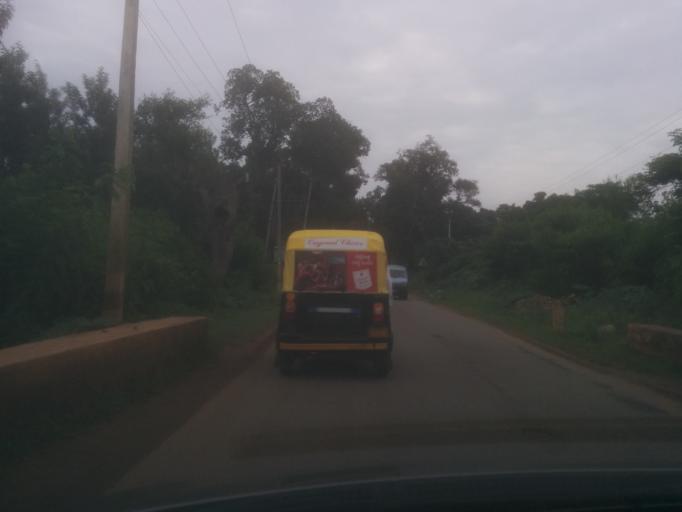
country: IN
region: Karnataka
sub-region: Chikmagalur
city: Chikmagalur
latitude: 13.3481
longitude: 75.7653
